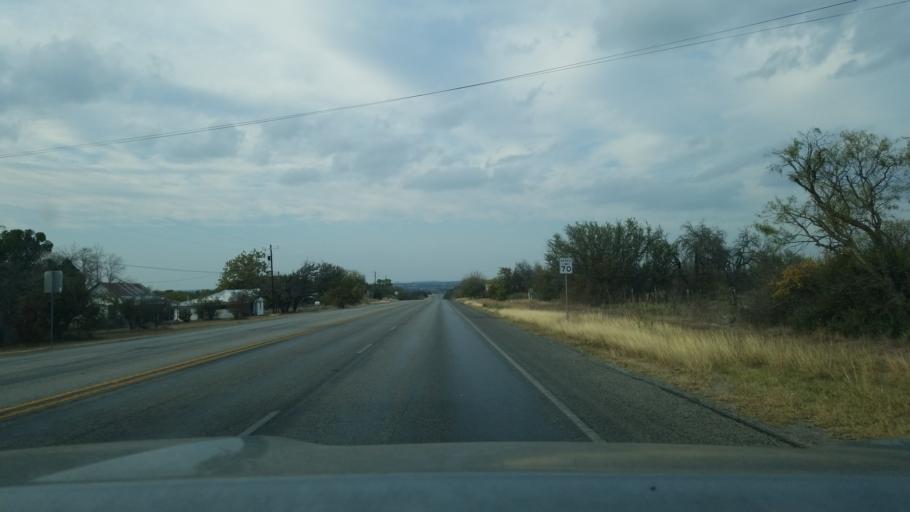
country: US
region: Texas
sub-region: Mills County
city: Goldthwaite
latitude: 31.4886
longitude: -98.5738
